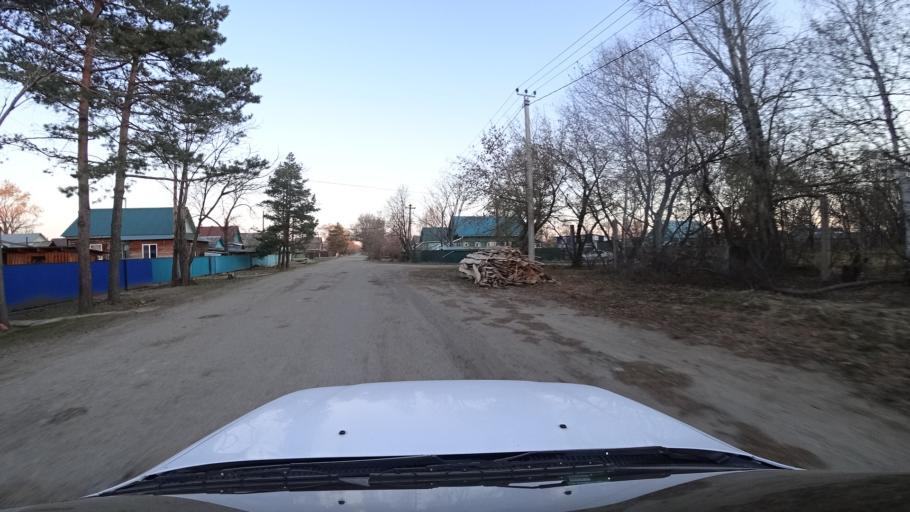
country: RU
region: Primorskiy
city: Dal'nerechensk
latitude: 45.9211
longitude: 133.7361
